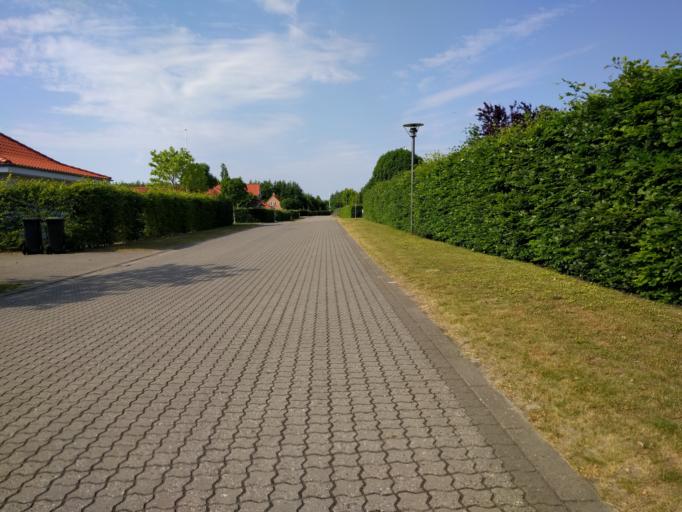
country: DK
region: South Denmark
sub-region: Kerteminde Kommune
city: Kerteminde
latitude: 55.4394
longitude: 10.6531
